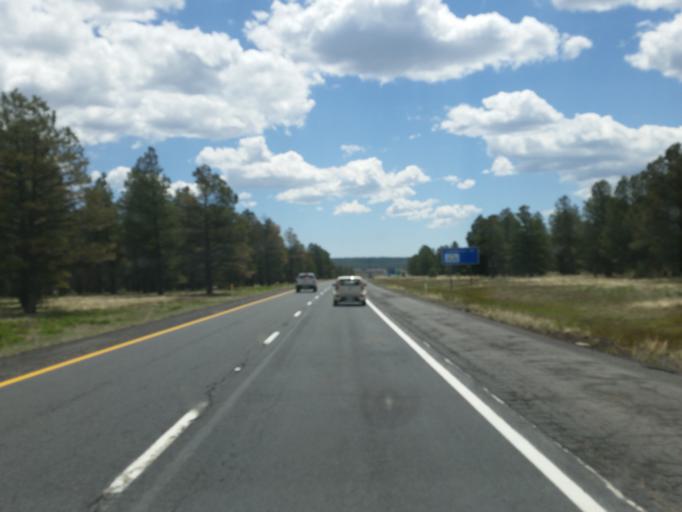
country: US
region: Arizona
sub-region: Coconino County
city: Parks
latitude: 35.2460
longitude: -111.8463
